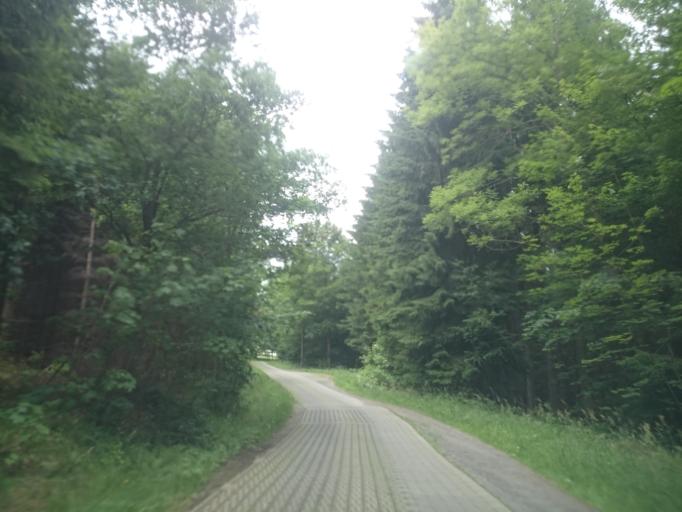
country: DE
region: Saxony
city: Bornichen
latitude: 50.7563
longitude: 13.1481
